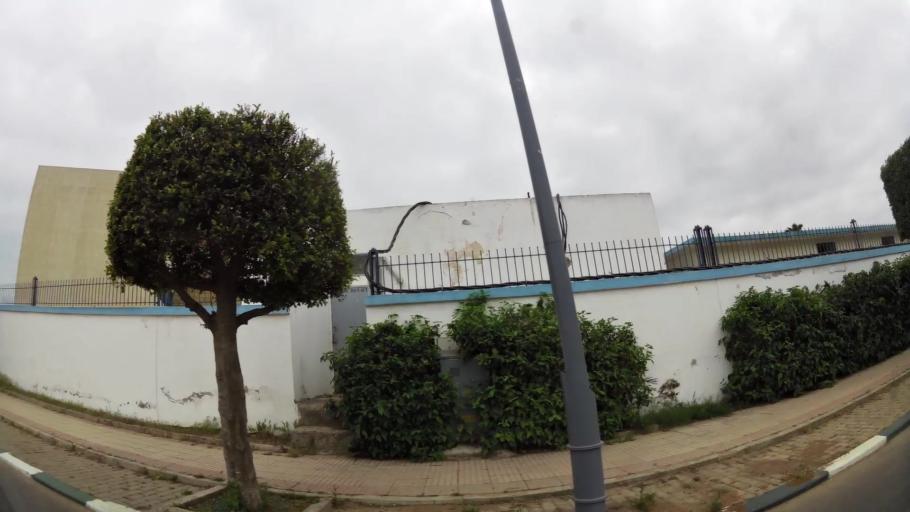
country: MA
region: Rabat-Sale-Zemmour-Zaer
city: Sale
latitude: 34.0304
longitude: -6.7975
